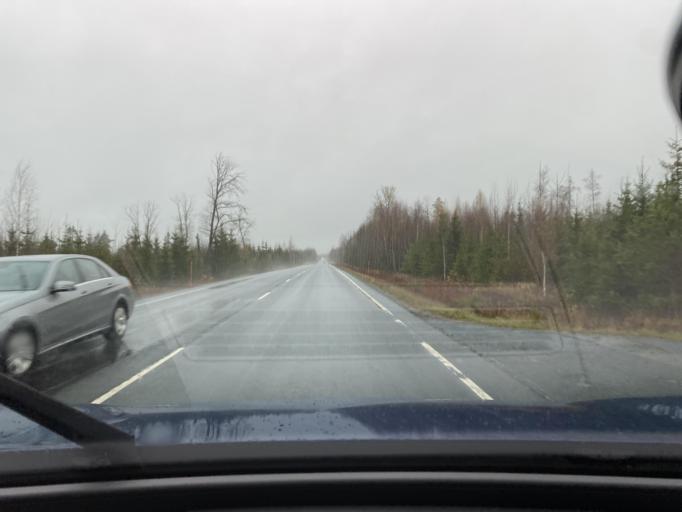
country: FI
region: Varsinais-Suomi
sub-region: Loimaa
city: Alastaro
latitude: 60.9023
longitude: 22.9395
